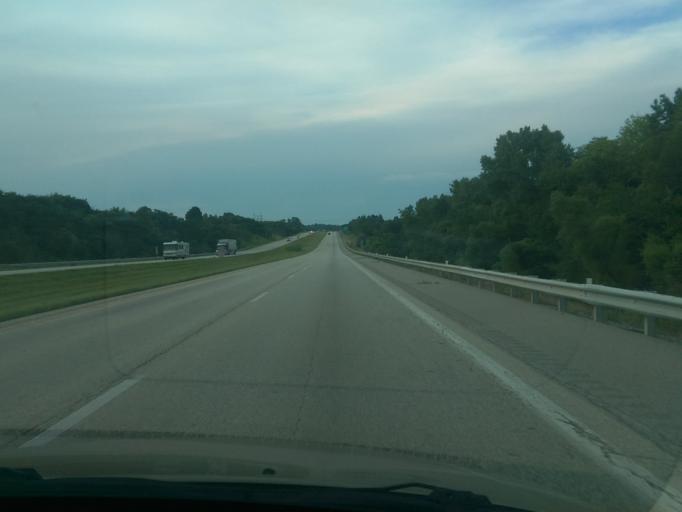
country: US
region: Missouri
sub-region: Andrew County
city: Country Club Village
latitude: 39.8362
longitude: -94.8051
